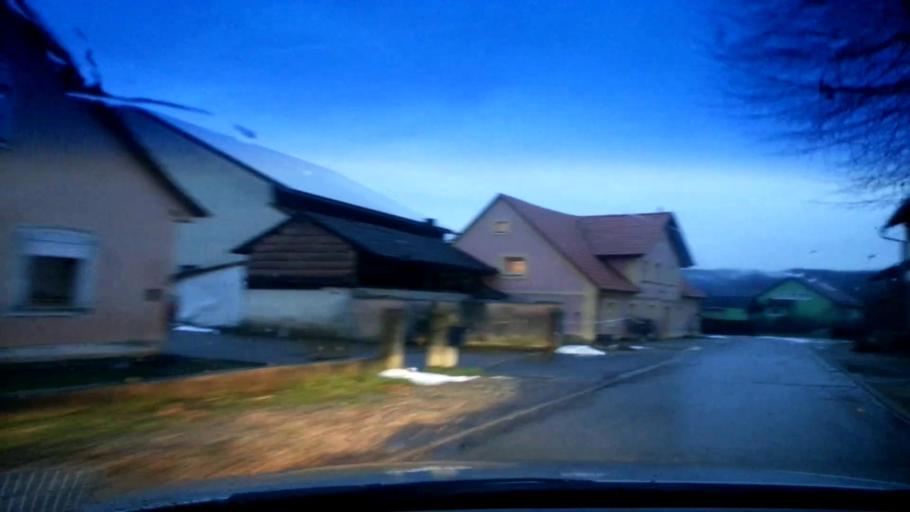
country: DE
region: Bavaria
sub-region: Upper Franconia
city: Memmelsdorf
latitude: 49.9721
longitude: 10.9839
